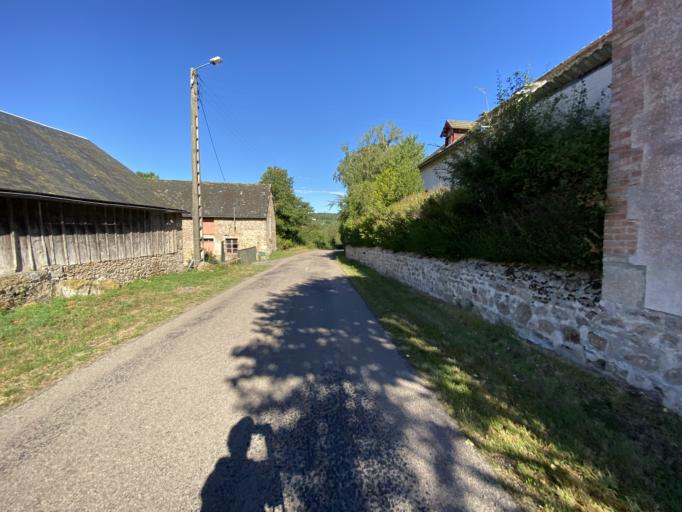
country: FR
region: Bourgogne
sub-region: Departement de la Cote-d'Or
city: Saulieu
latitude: 47.2584
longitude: 4.1828
